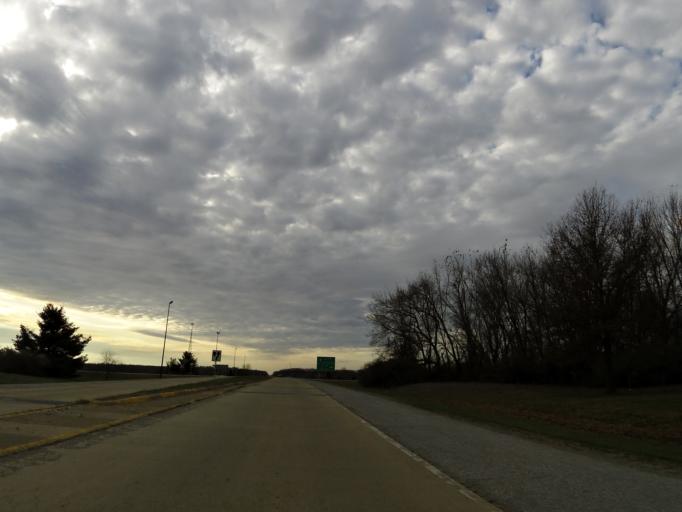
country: US
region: Illinois
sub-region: Jefferson County
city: Mount Vernon
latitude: 38.3653
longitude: -89.0347
